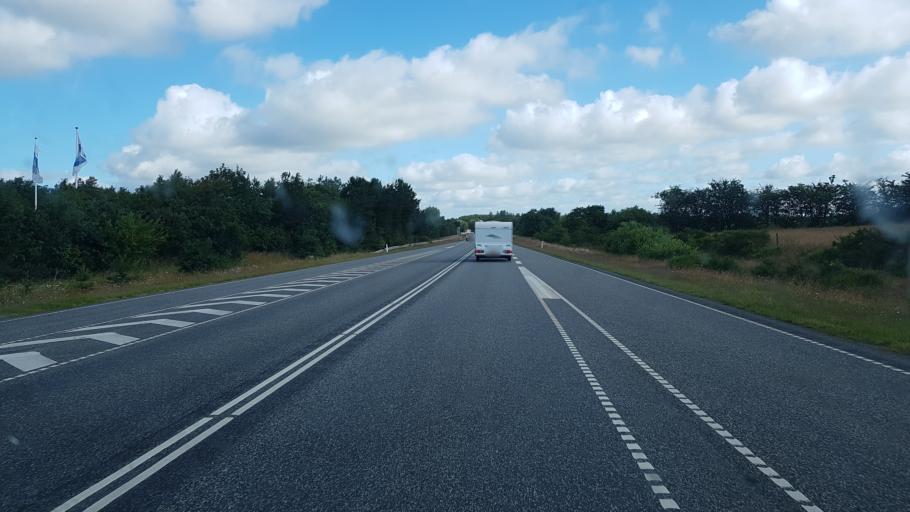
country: DK
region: South Denmark
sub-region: Varde Kommune
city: Varde
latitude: 55.6299
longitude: 8.5156
